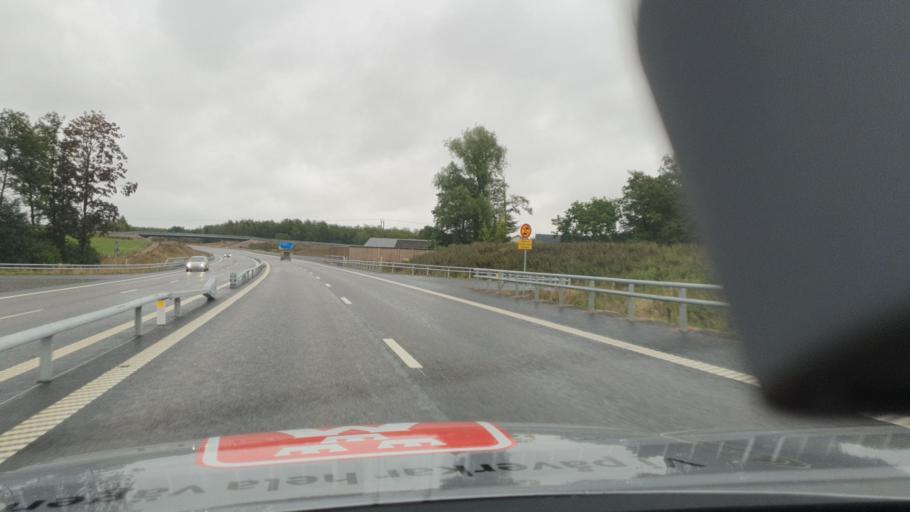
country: SE
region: Skane
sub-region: Kristianstads Kommun
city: Norra Asum
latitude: 55.9709
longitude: 14.0670
